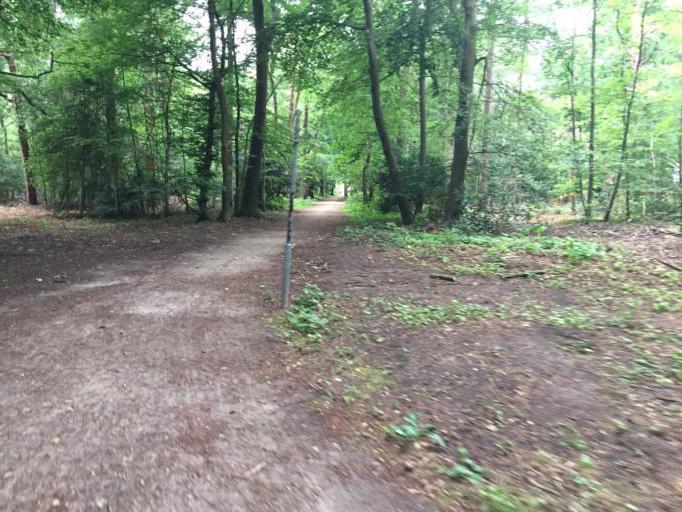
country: NL
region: Utrecht
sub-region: Gemeente Zeist
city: Zeist
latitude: 52.0880
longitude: 5.2580
